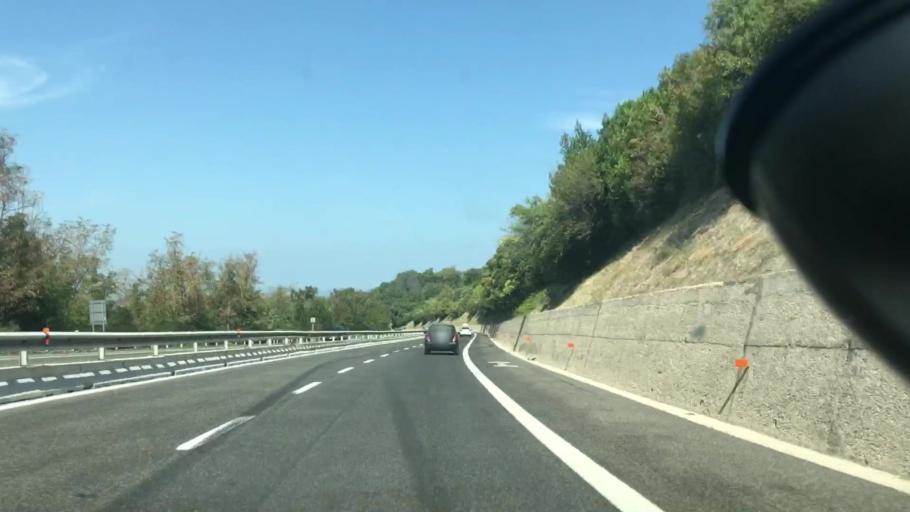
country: IT
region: Abruzzo
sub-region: Provincia di Chieti
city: Vasto
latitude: 42.1381
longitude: 14.6607
